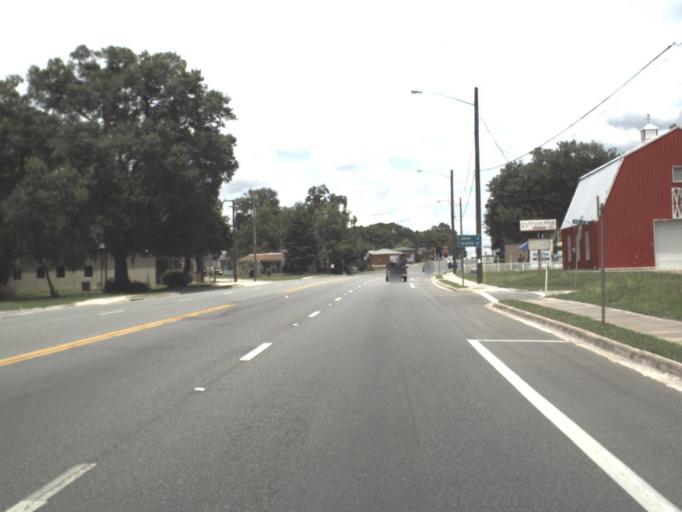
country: US
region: Florida
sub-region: Suwannee County
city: Live Oak
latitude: 30.3014
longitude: -82.9819
